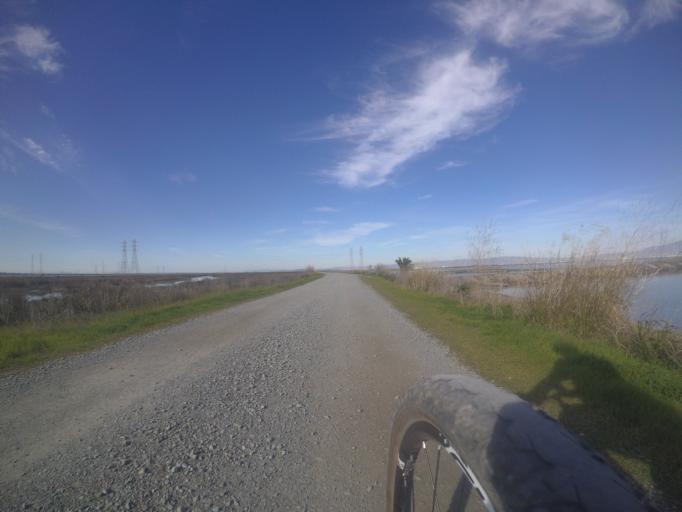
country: US
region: California
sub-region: Santa Clara County
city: Mountain View
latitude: 37.4388
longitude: -122.0679
